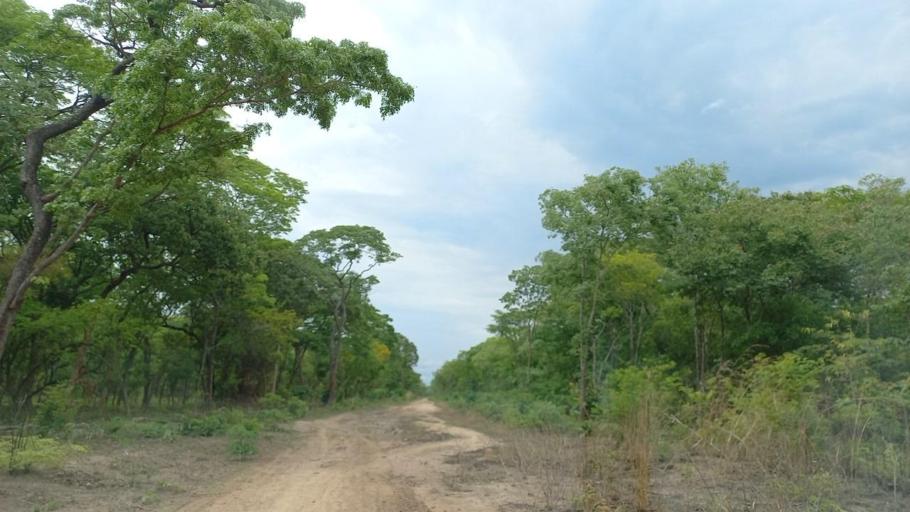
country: ZM
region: North-Western
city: Kalengwa
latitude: -13.5545
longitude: 24.9746
